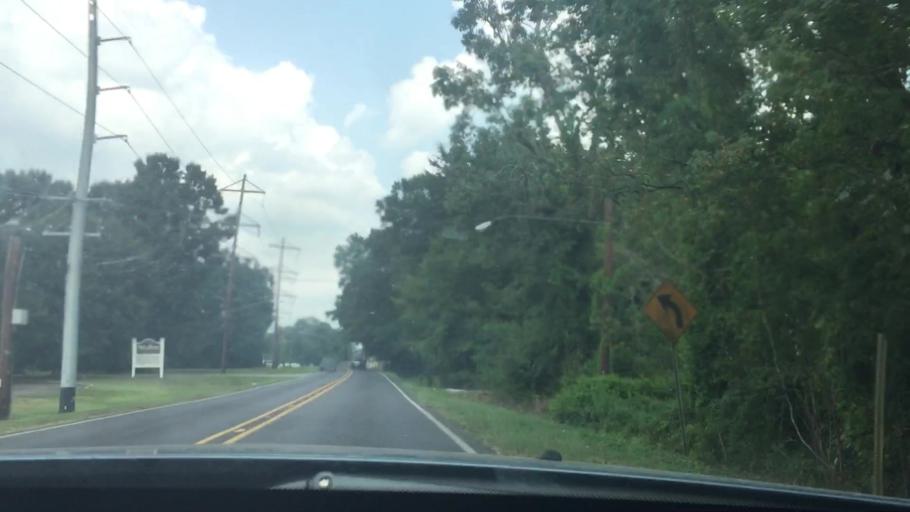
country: US
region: Louisiana
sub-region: East Baton Rouge Parish
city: Monticello
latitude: 30.4408
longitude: -91.0443
